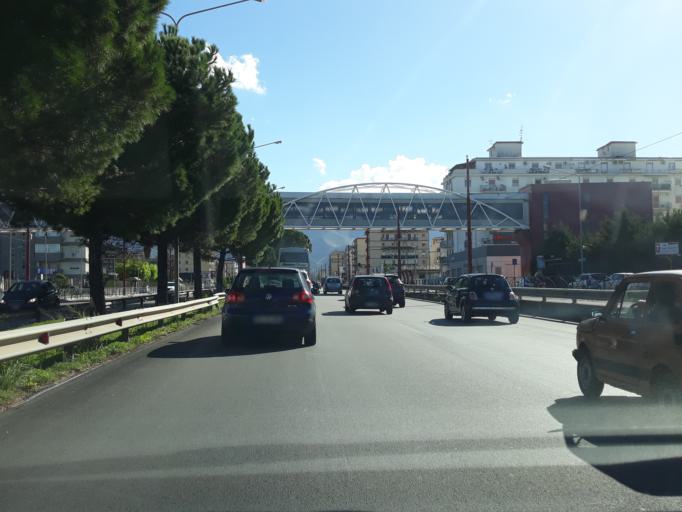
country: IT
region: Sicily
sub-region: Palermo
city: Palermo
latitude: 38.1167
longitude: 13.3290
